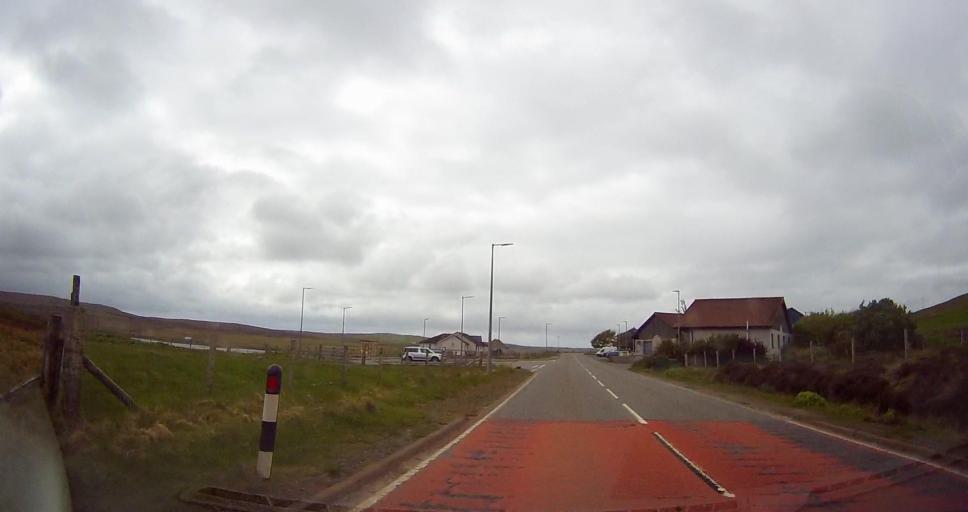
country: GB
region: Scotland
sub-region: Shetland Islands
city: Lerwick
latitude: 60.2529
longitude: -1.3954
